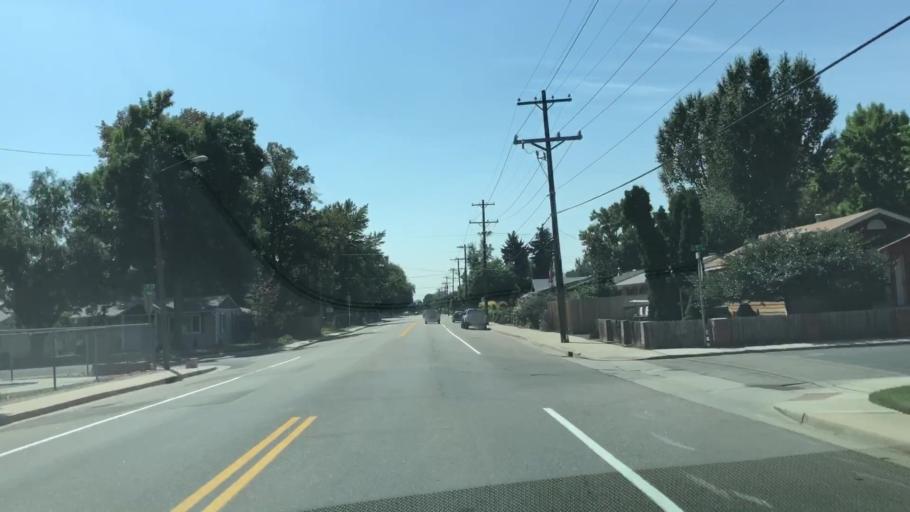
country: US
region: Colorado
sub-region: Larimer County
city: Loveland
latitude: 40.3969
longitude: -105.0589
